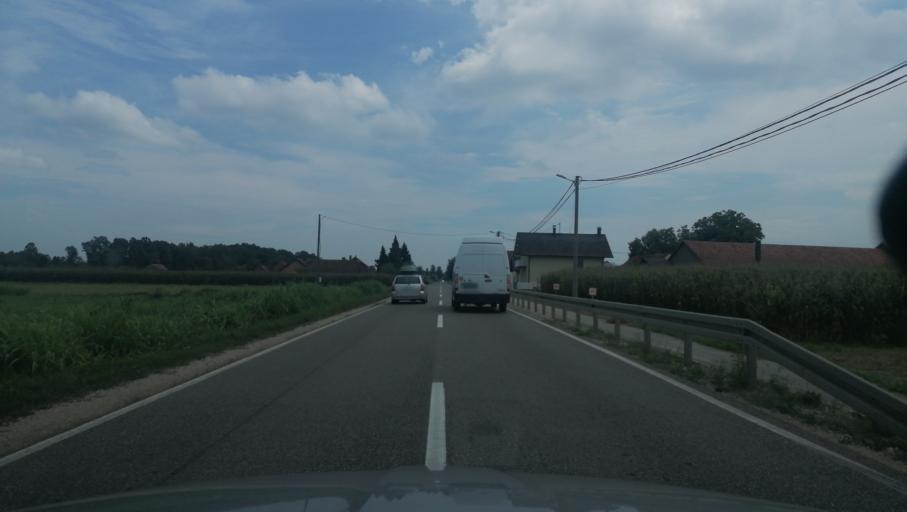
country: BA
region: Republika Srpska
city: Obudovac
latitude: 44.9563
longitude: 18.6351
